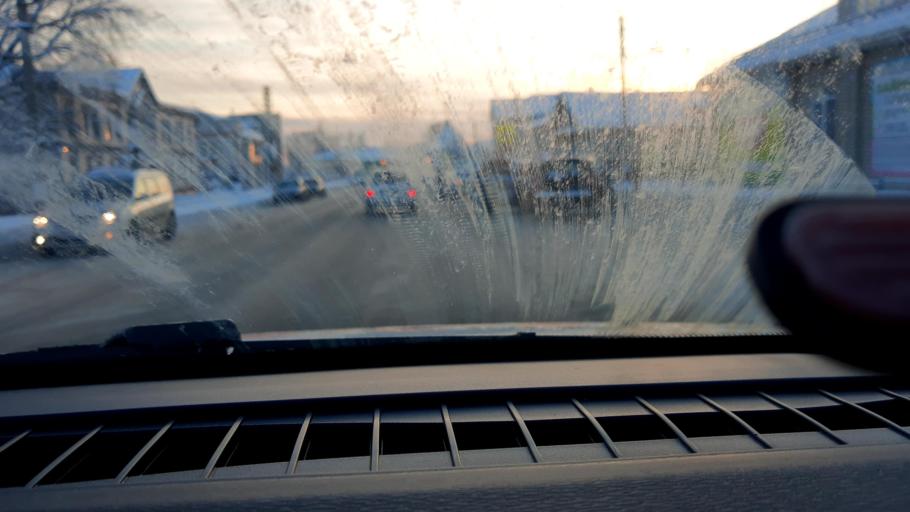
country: RU
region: Nizjnij Novgorod
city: Uren'
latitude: 57.4552
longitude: 45.7835
